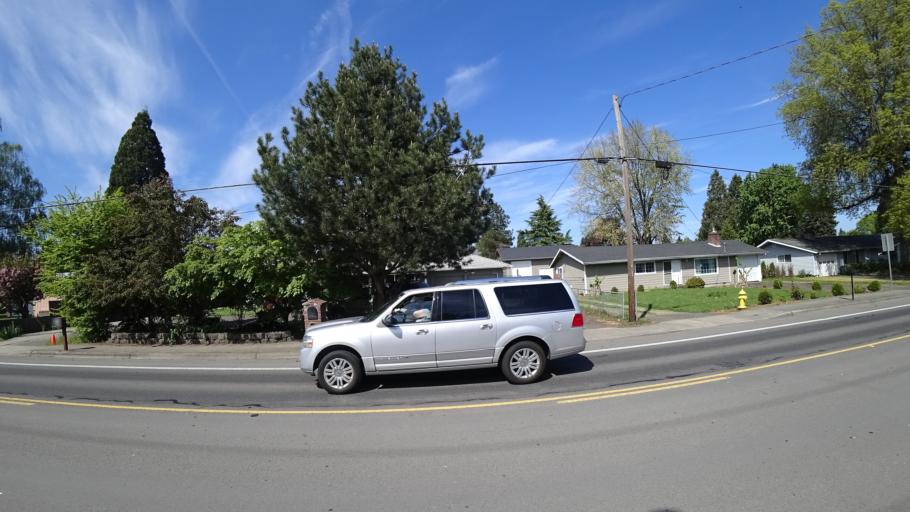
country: US
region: Oregon
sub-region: Washington County
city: Hillsboro
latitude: 45.5202
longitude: -122.9513
